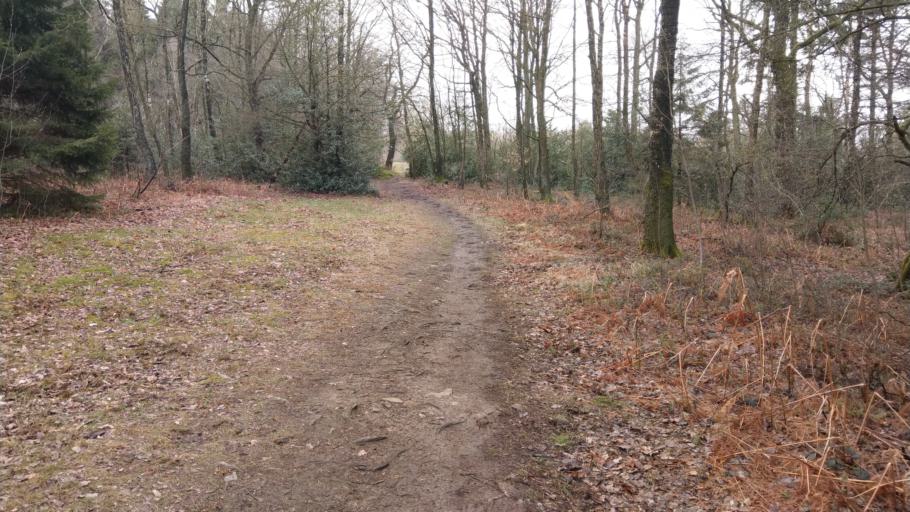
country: BE
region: Wallonia
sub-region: Province de Liege
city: Raeren
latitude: 50.6703
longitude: 6.1478
